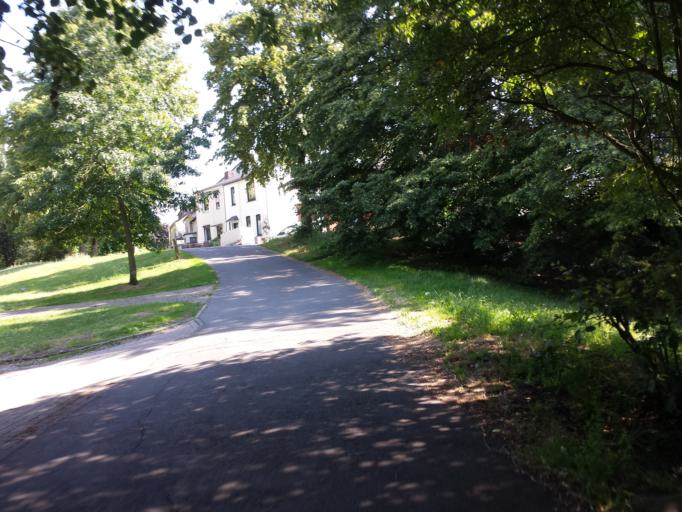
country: DE
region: Bremen
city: Bremen
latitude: 53.0916
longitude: 8.7611
